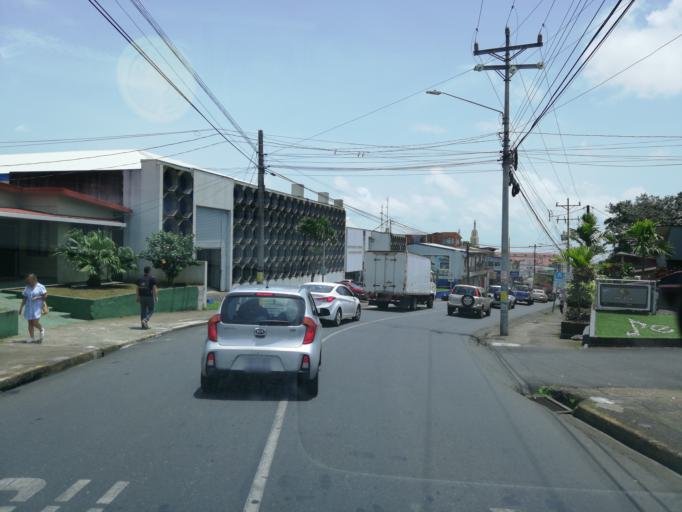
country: CR
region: Alajuela
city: Quesada
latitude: 10.3203
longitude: -84.4295
